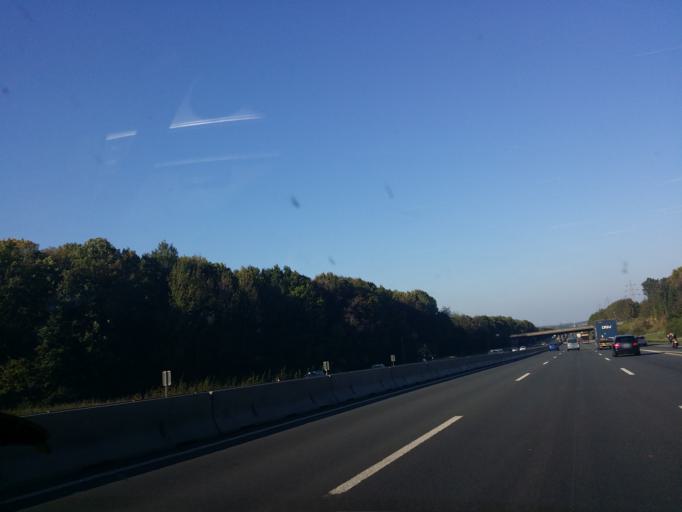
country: DE
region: North Rhine-Westphalia
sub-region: Regierungsbezirk Arnsberg
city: Unna
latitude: 51.5274
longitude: 7.6594
